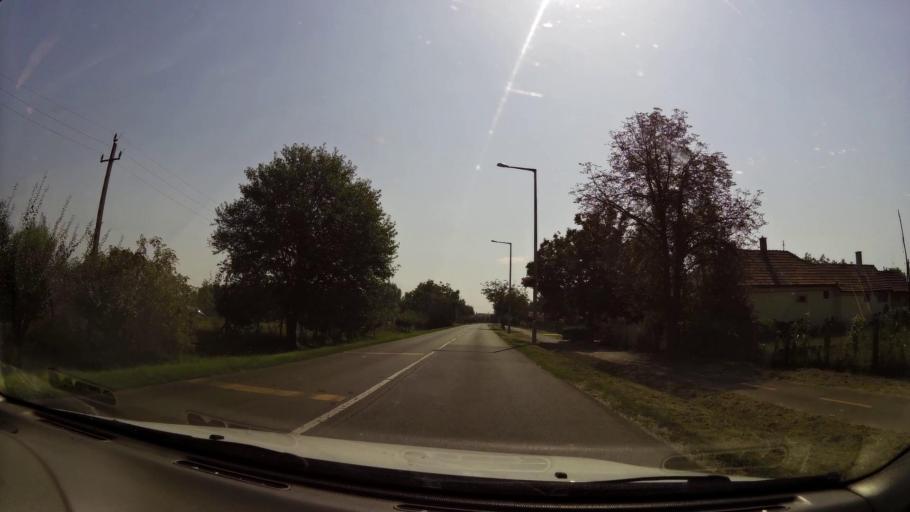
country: HU
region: Pest
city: Ujszilvas
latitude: 47.2779
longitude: 19.9245
